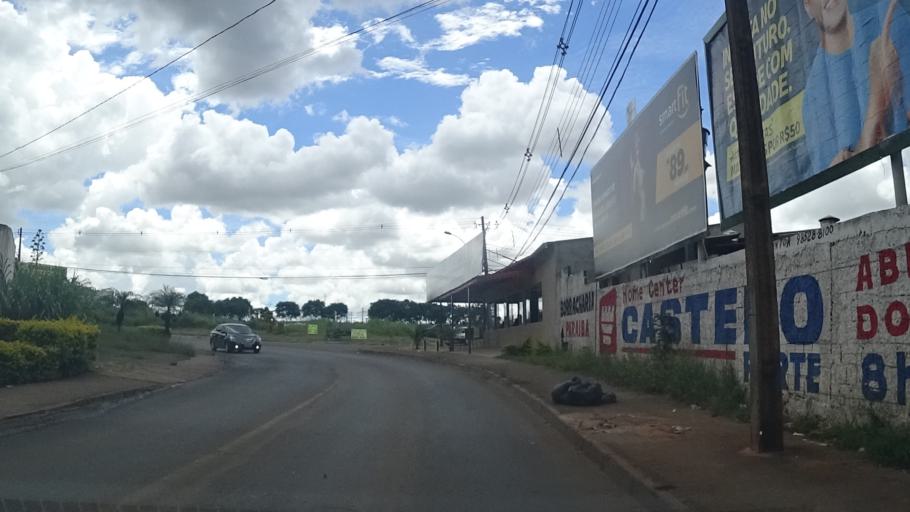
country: BR
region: Federal District
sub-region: Brasilia
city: Brasilia
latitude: -15.8487
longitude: -48.0278
